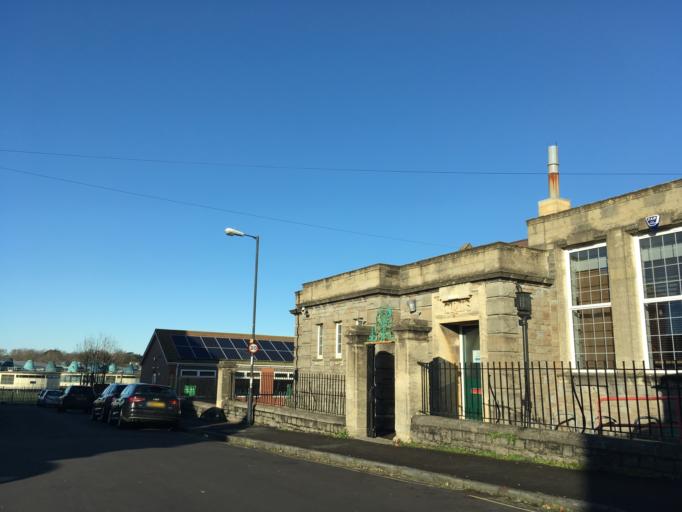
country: GB
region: England
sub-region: South Gloucestershire
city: Mangotsfield
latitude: 51.4786
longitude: -2.5365
